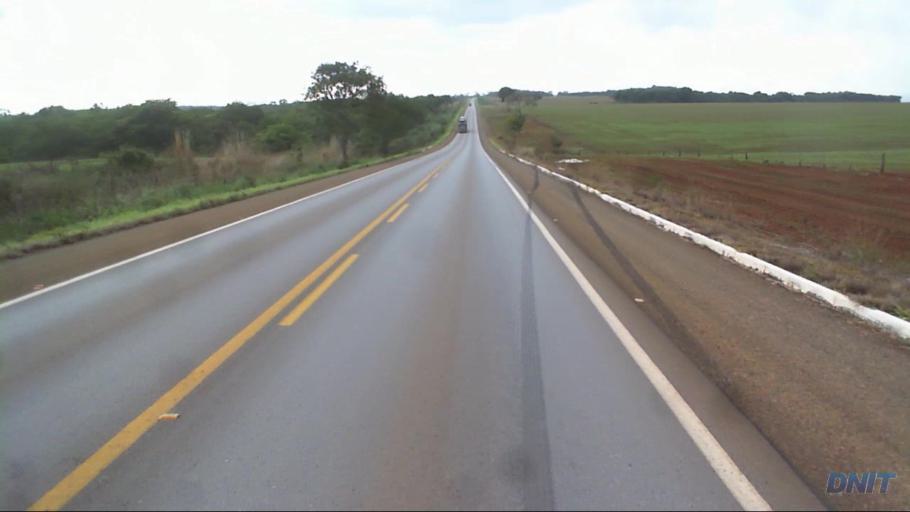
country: BR
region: Goias
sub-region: Uruacu
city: Uruacu
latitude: -14.6674
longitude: -49.1481
